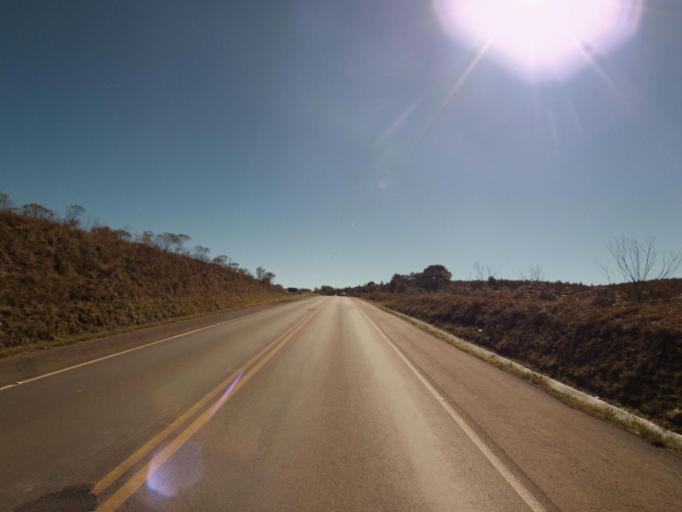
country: BR
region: Santa Catarina
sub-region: Concordia
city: Concordia
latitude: -26.9272
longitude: -51.8761
